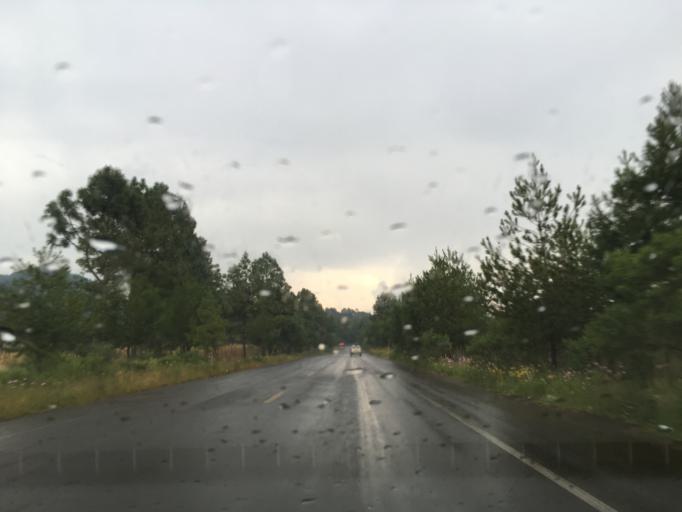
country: MX
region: Michoacan
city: Angahuan
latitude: 19.5380
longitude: -102.1994
